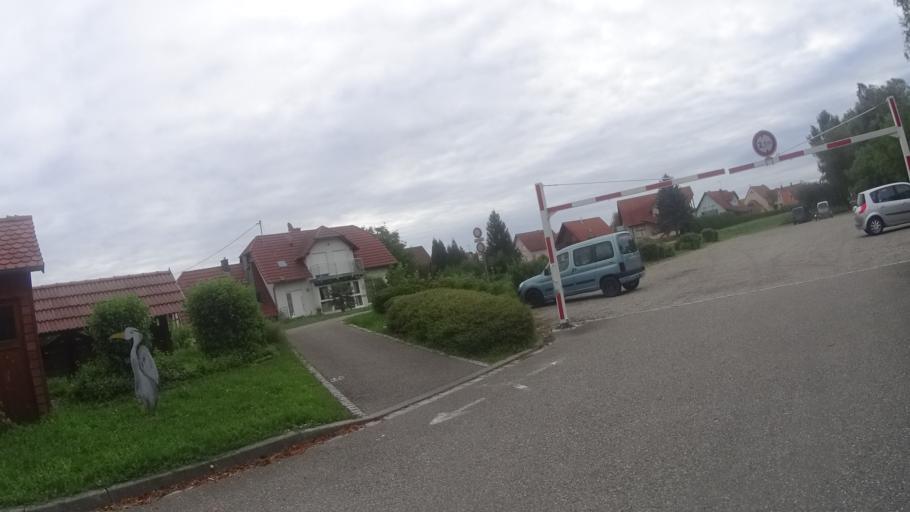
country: FR
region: Alsace
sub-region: Departement du Bas-Rhin
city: Seltz
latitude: 48.9185
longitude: 8.1487
